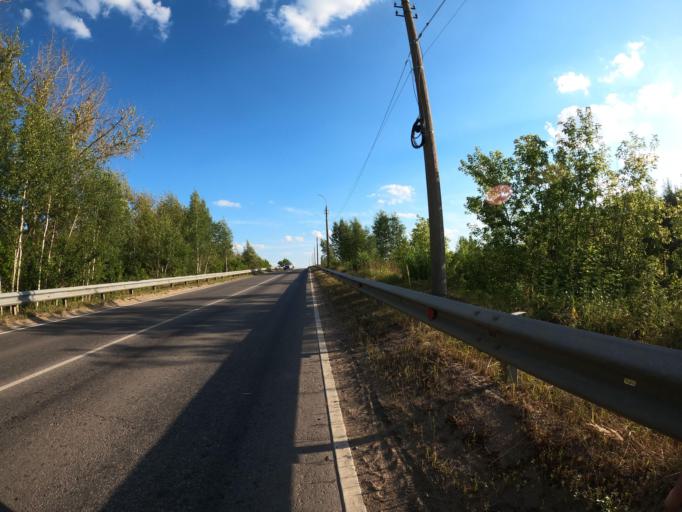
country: RU
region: Moskovskaya
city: Raduzhnyy
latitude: 55.1491
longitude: 38.7303
